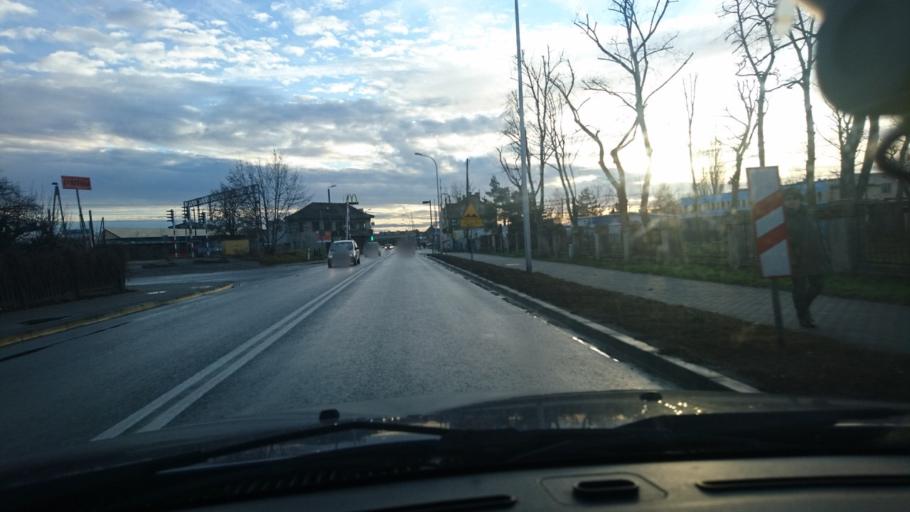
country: PL
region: Greater Poland Voivodeship
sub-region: Powiat kepinski
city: Kepno
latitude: 51.2909
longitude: 17.9944
